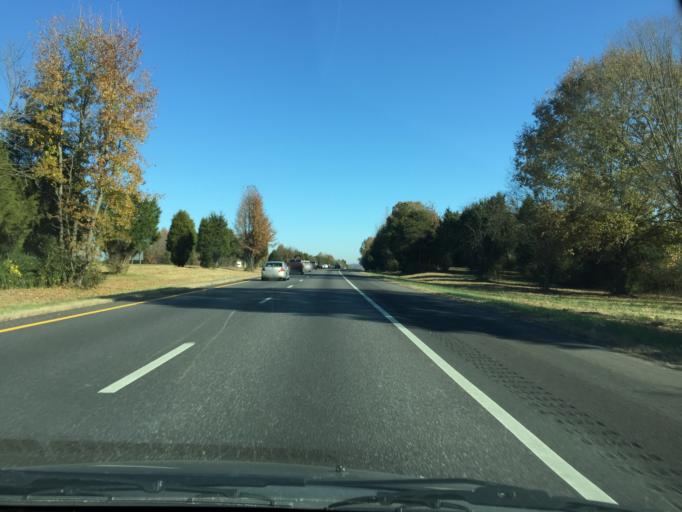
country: US
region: Tennessee
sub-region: Monroe County
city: Sweetwater
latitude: 35.6131
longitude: -84.5020
